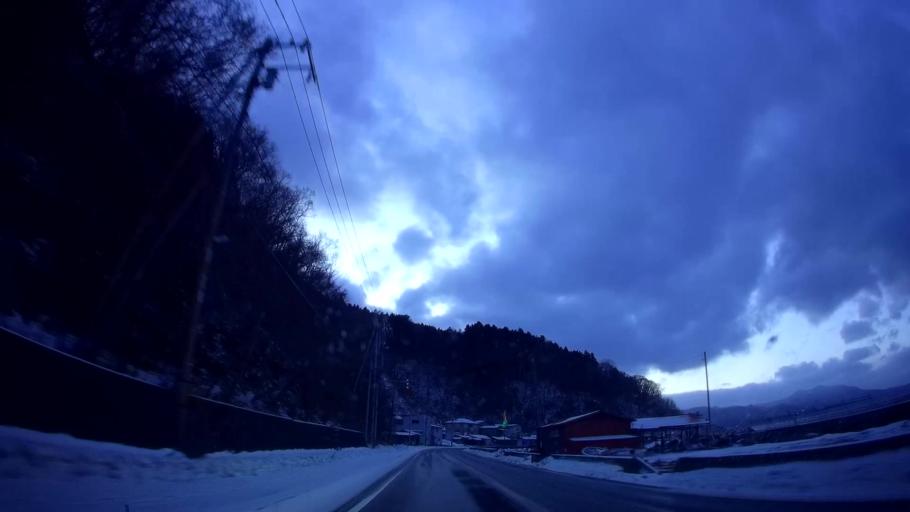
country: JP
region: Hokkaido
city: Hakodate
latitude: 41.8932
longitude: 141.0442
